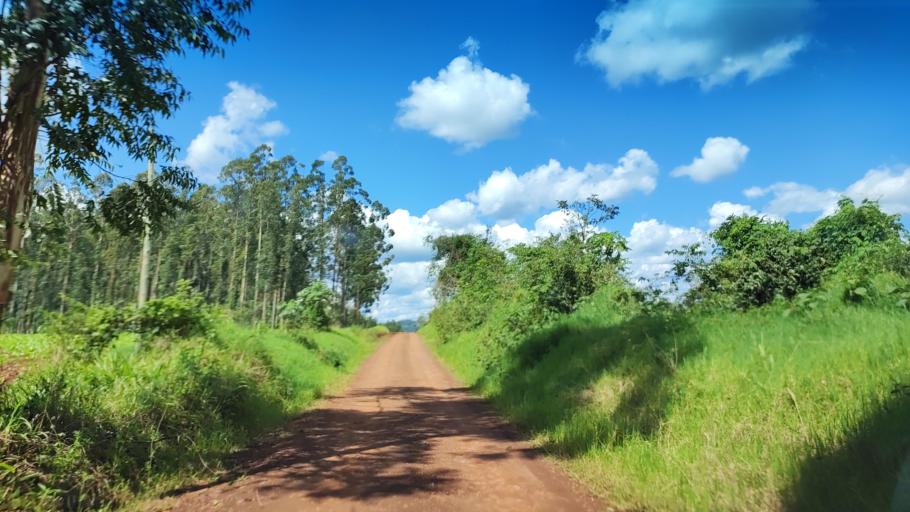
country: AR
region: Misiones
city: Ruiz de Montoya
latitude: -26.9528
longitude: -55.0205
